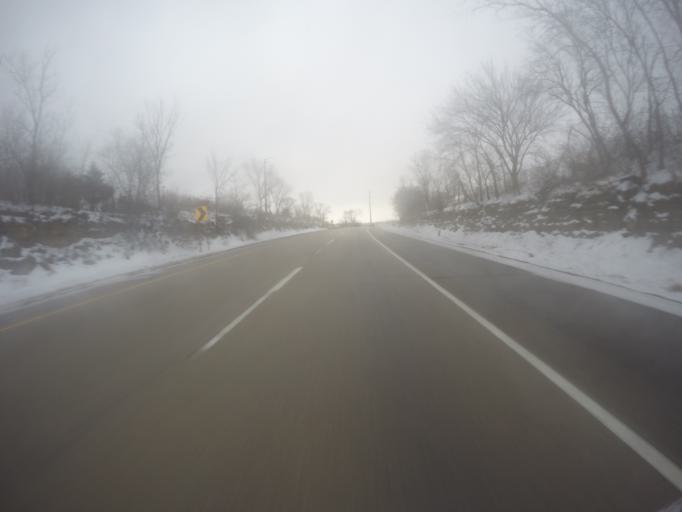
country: US
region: Minnesota
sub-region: Goodhue County
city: Cannon Falls
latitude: 44.4483
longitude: -92.8958
